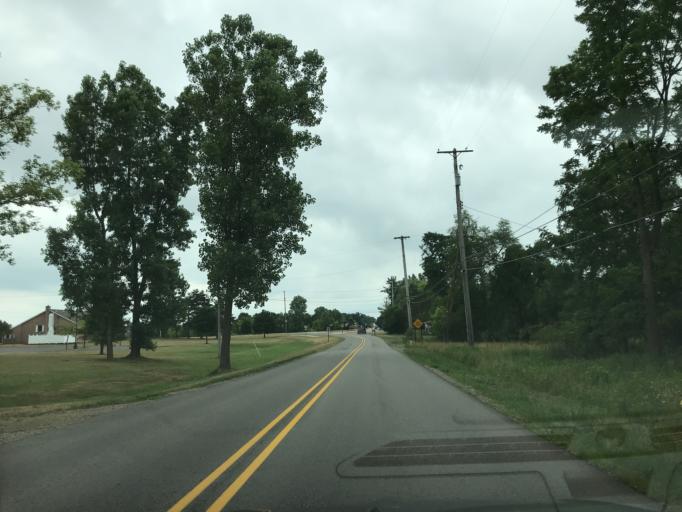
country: US
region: Michigan
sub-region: Eaton County
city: Waverly
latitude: 42.7574
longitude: -84.6618
